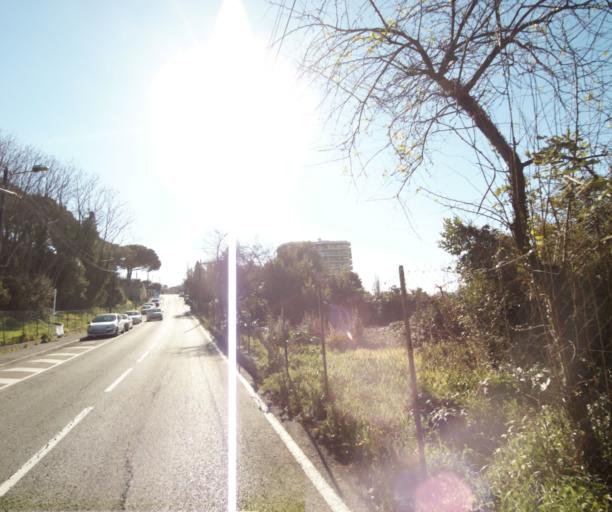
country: FR
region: Provence-Alpes-Cote d'Azur
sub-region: Departement des Alpes-Maritimes
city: Antibes
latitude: 43.5907
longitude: 7.1109
